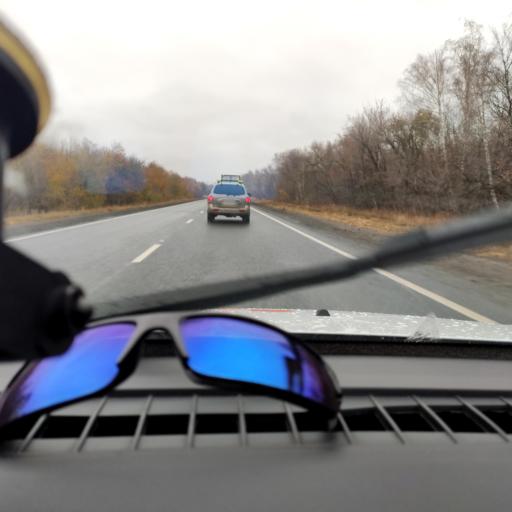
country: RU
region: Samara
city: Novokuybyshevsk
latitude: 52.9824
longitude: 49.9041
